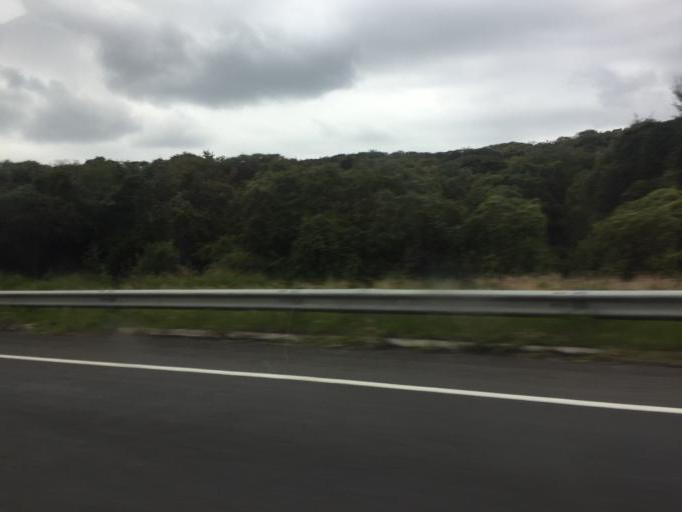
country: MX
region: Jalisco
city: Ocotlan
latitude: 20.4310
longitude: -102.7849
